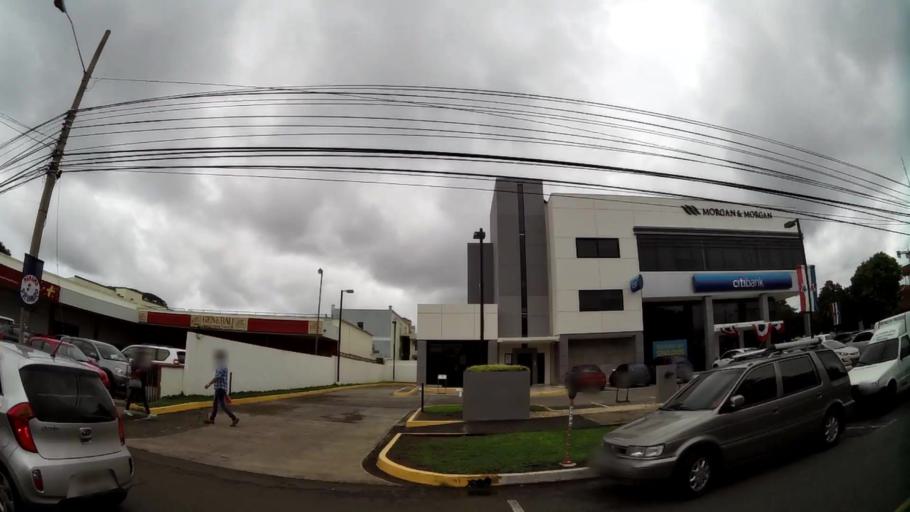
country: PA
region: Chiriqui
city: David
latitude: 8.4303
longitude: -82.4280
